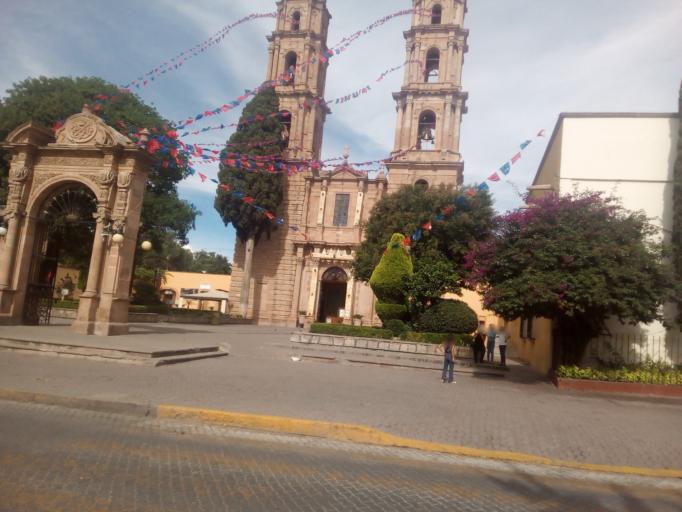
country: MX
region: Guanajuato
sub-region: San Luis de la Paz
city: San Luis de la Paz
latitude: 21.2984
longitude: -100.5145
